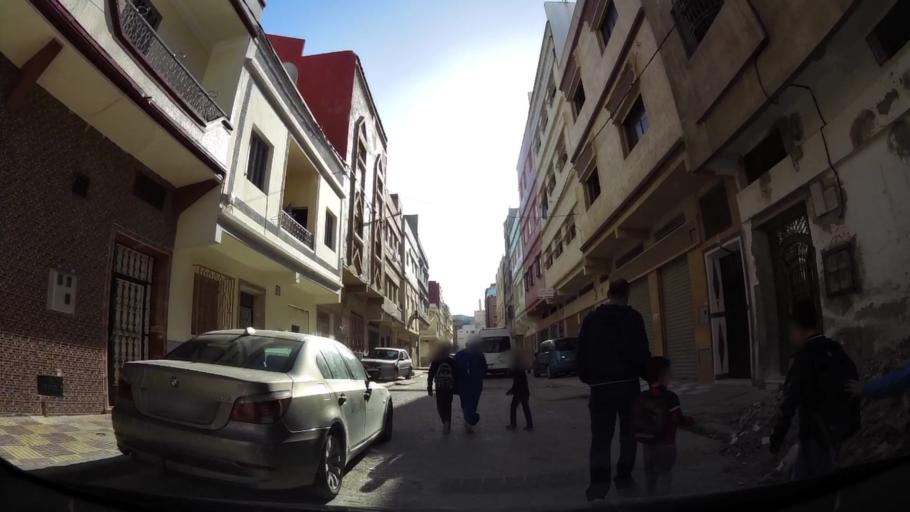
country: MA
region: Tanger-Tetouan
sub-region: Tanger-Assilah
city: Tangier
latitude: 35.7506
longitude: -5.8000
